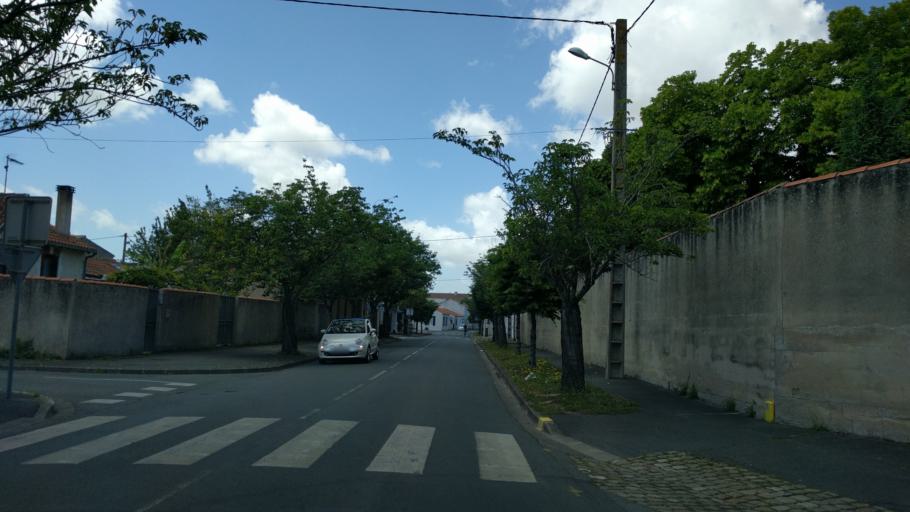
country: FR
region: Poitou-Charentes
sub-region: Departement de la Charente-Maritime
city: La Rochelle
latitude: 46.1629
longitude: -1.1342
